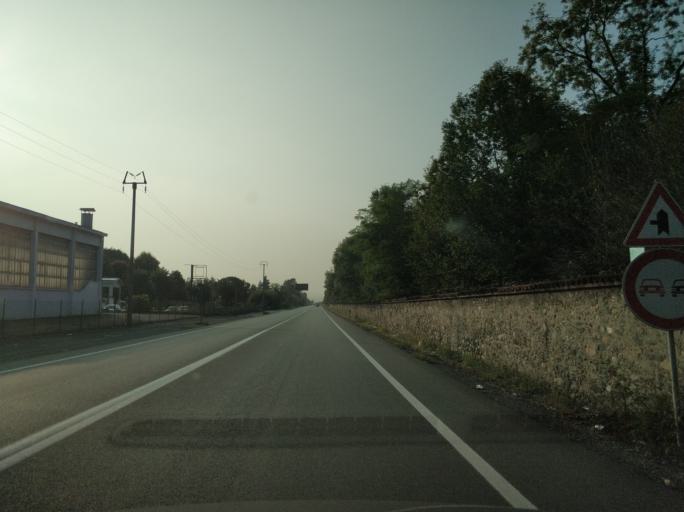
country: IT
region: Piedmont
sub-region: Provincia di Torino
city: Robassomero
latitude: 45.2070
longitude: 7.5505
